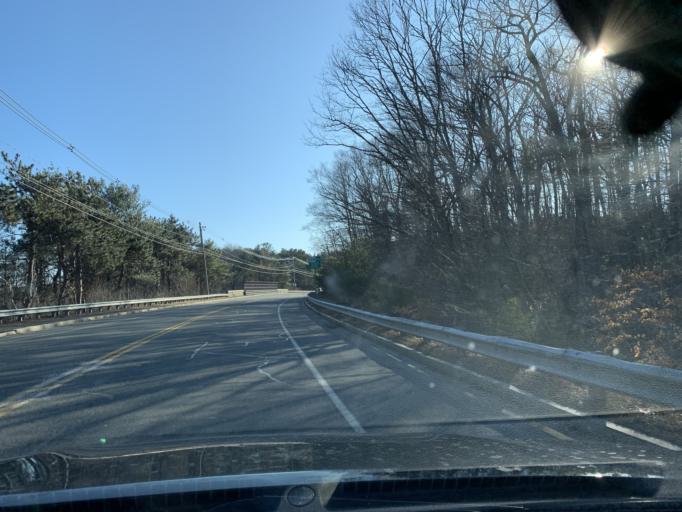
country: US
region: Massachusetts
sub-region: Essex County
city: Essex
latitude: 42.5912
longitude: -70.7653
